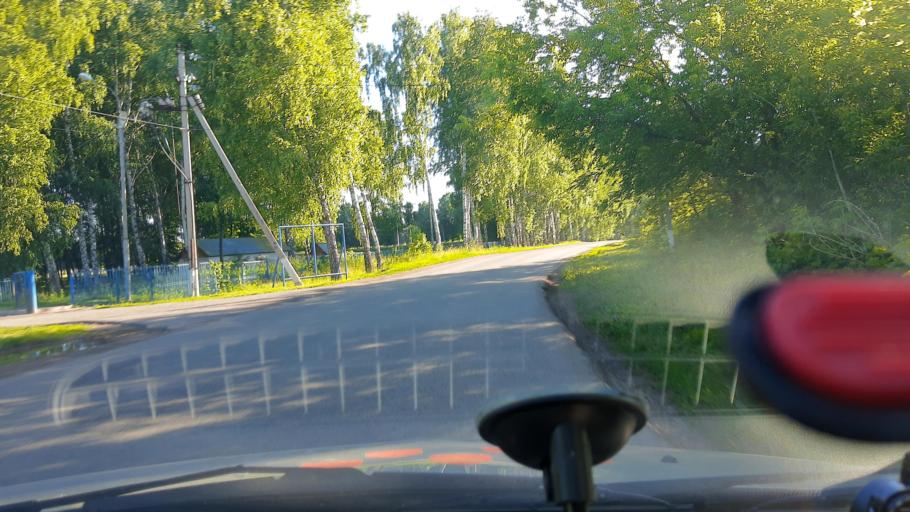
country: RU
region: Bashkortostan
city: Chishmy
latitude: 54.5989
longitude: 55.3754
